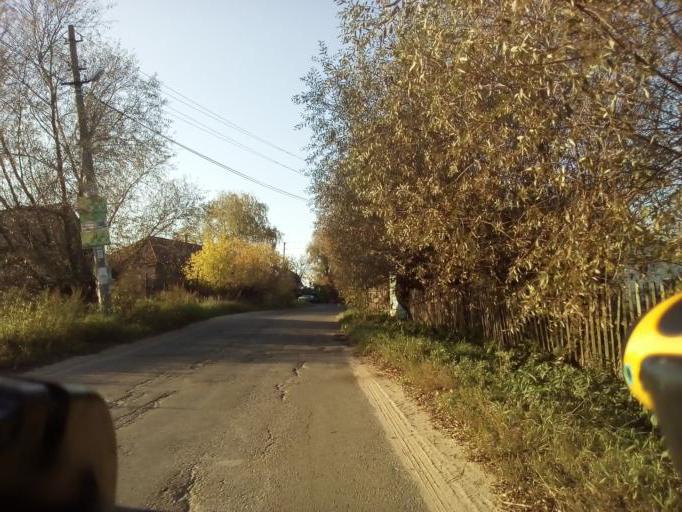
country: RU
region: Moskovskaya
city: Ramenskoye
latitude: 55.6118
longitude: 38.2953
